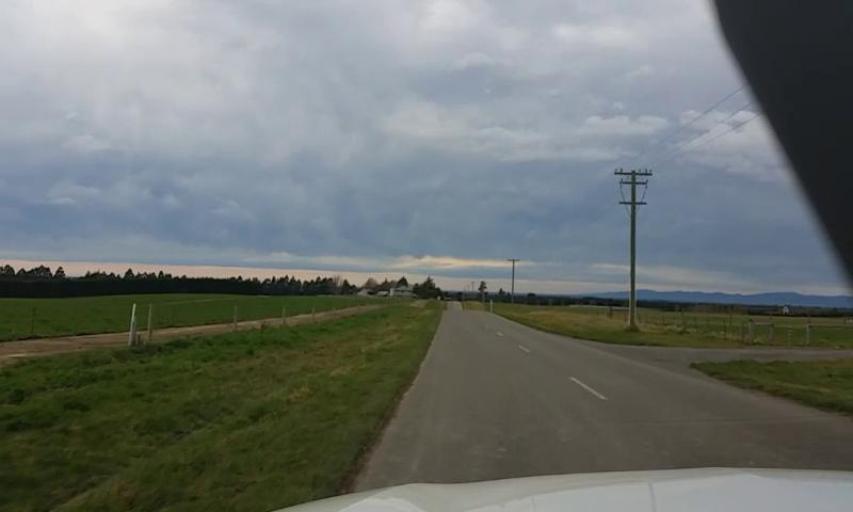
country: NZ
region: Canterbury
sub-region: Waimakariri District
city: Kaiapoi
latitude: -43.2969
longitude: 172.4768
